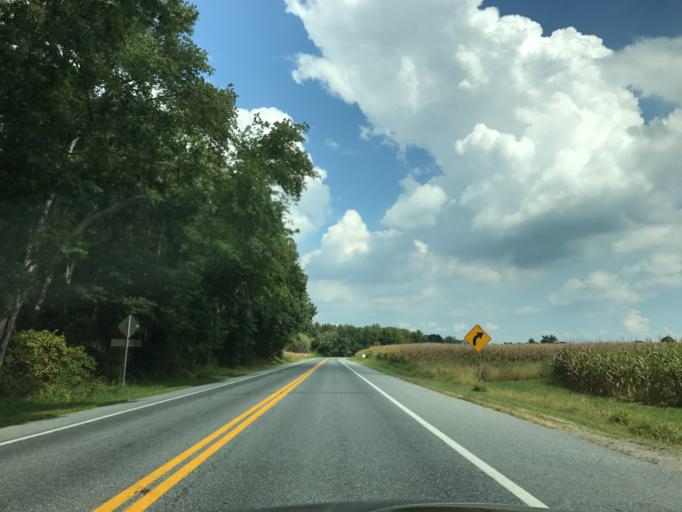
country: US
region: Delaware
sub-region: Kent County
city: Clayton
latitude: 39.1969
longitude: -75.7584
